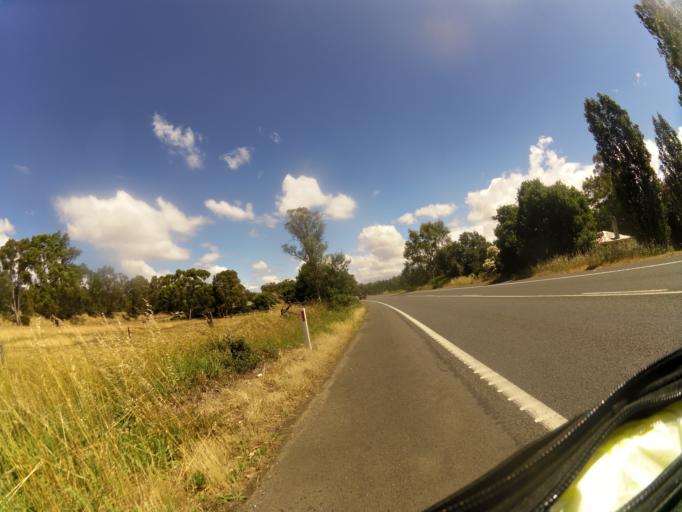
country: AU
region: Victoria
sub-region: Mount Alexander
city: Castlemaine
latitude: -37.0161
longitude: 144.2413
